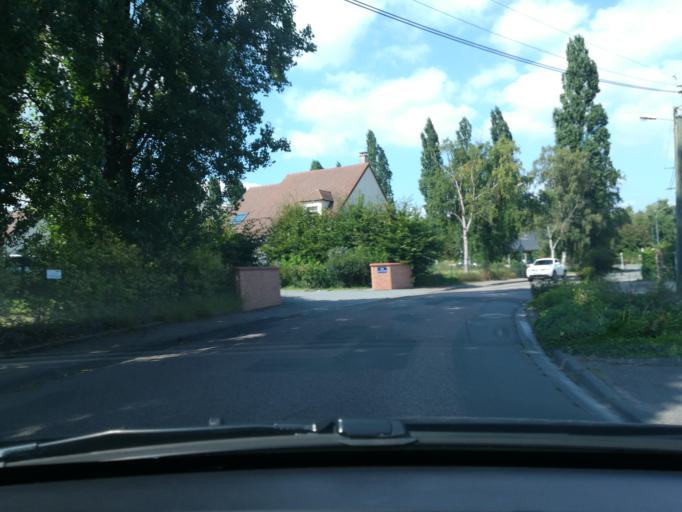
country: FR
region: Haute-Normandie
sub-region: Departement de la Seine-Maritime
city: Bois-Guillaume
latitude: 49.4682
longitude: 1.1262
